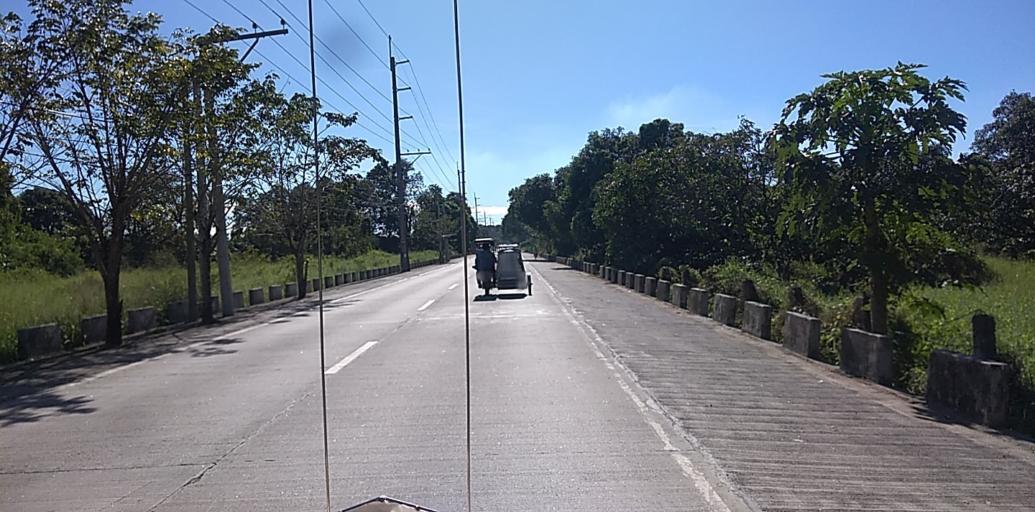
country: PH
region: Central Luzon
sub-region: Province of Pampanga
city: Santo Domingo
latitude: 15.0706
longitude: 120.7633
